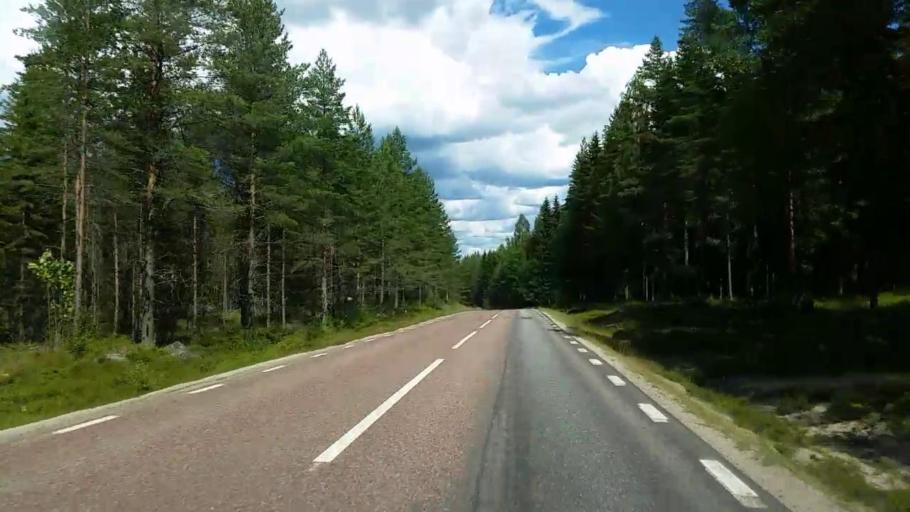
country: SE
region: Gaevleborg
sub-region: Ovanakers Kommun
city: Edsbyn
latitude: 61.3218
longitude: 15.5140
